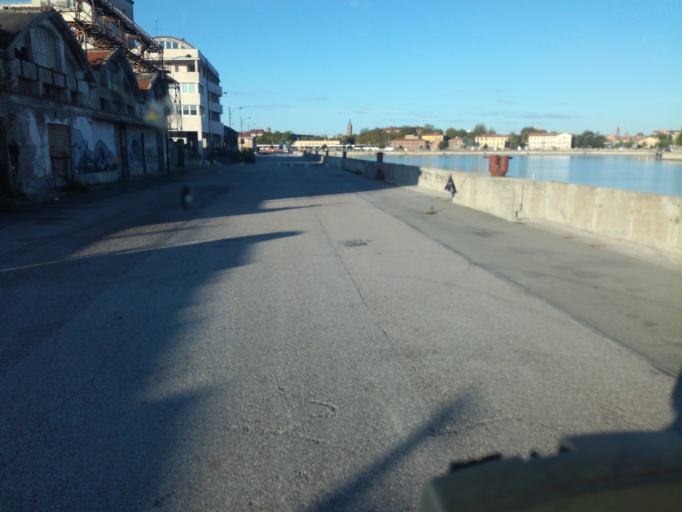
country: IT
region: Emilia-Romagna
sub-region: Provincia di Ravenna
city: Ravenna
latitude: 44.4218
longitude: 12.2133
